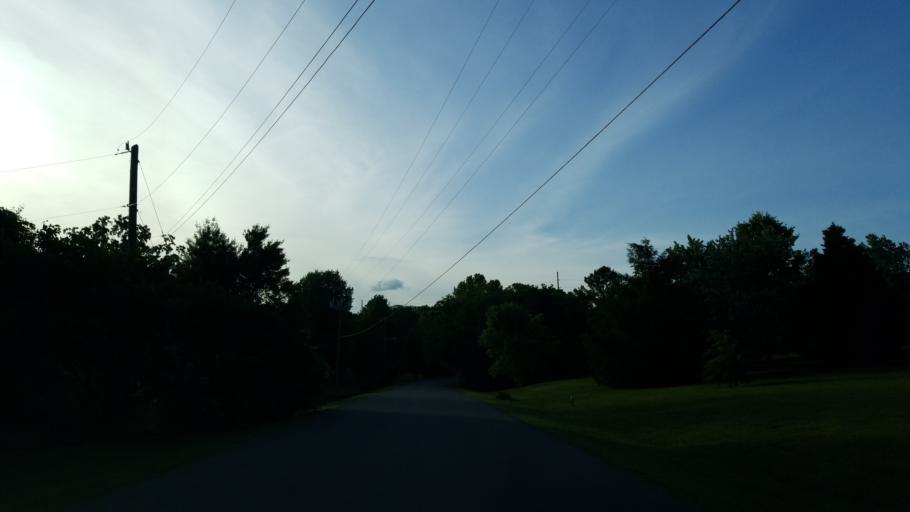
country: US
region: Tennessee
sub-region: Davidson County
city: Forest Hills
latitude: 36.0414
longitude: -86.8416
